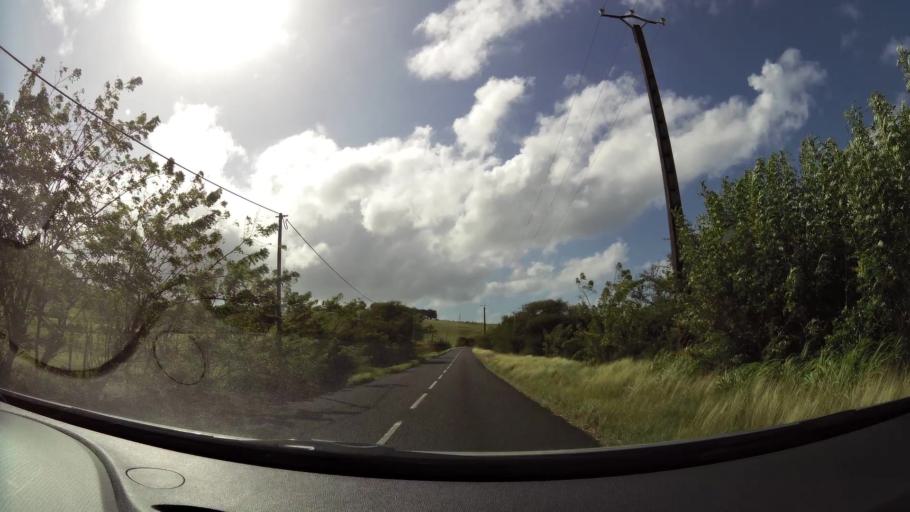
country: MQ
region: Martinique
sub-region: Martinique
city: Le Marin
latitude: 14.4163
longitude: -60.8780
